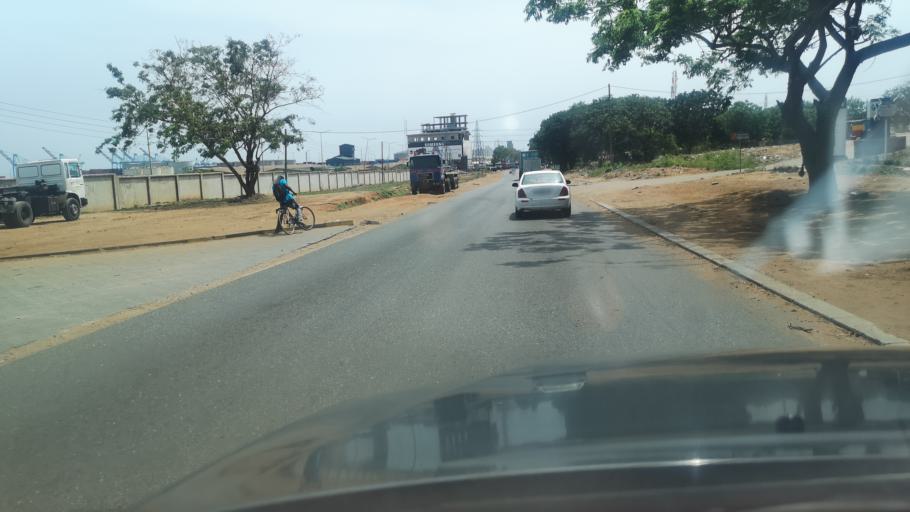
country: GH
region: Greater Accra
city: Tema
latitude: 5.6335
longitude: -0.0025
